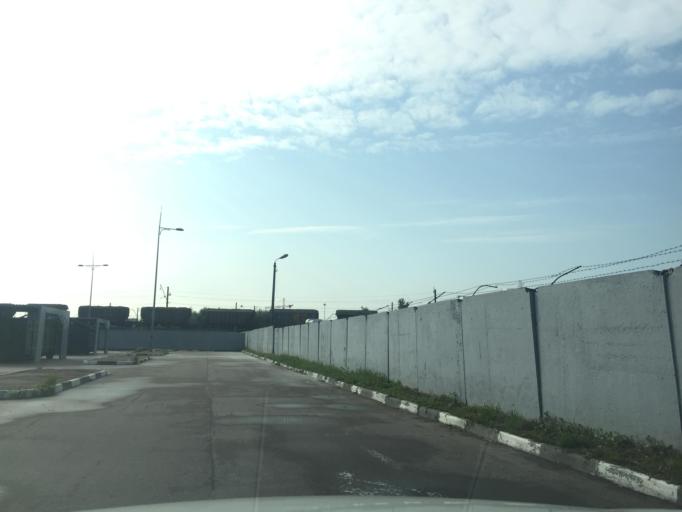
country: RU
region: St.-Petersburg
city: Kupchino
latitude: 59.8192
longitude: 30.3130
